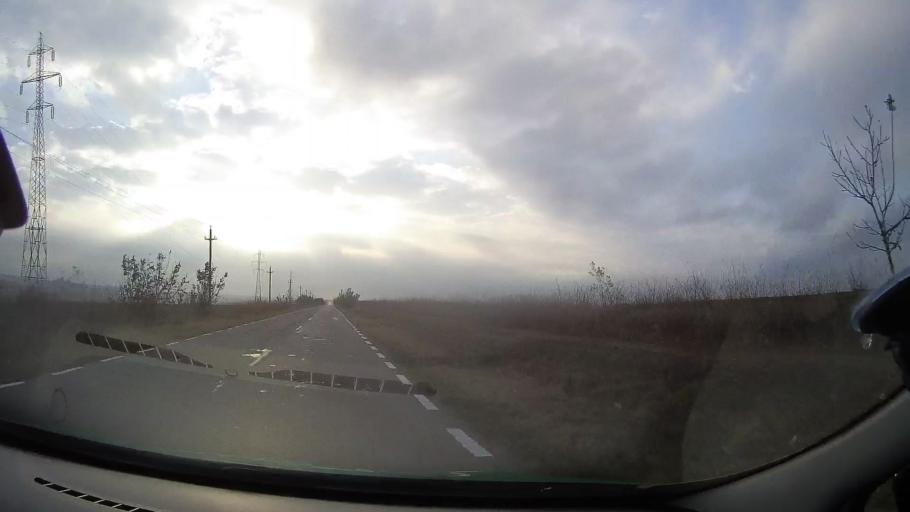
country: RO
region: Constanta
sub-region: Comuna Pestera
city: Pestera
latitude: 44.2139
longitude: 28.1846
